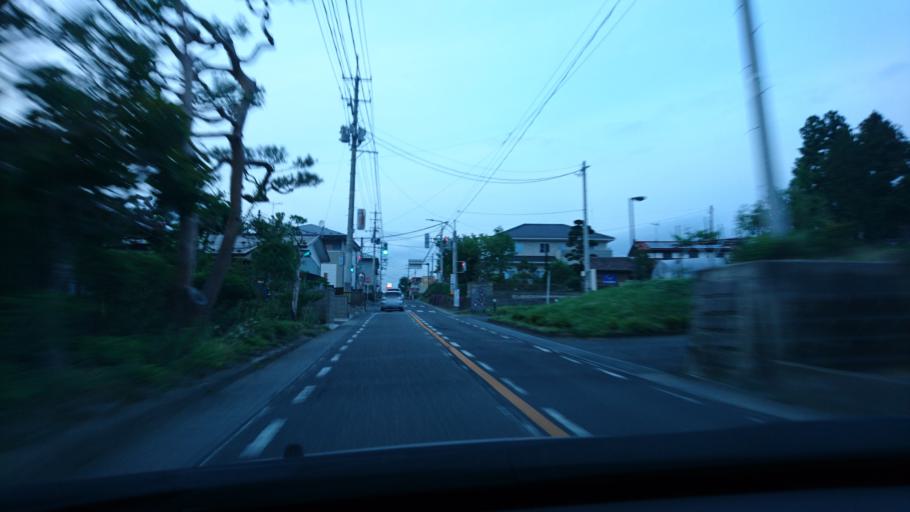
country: JP
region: Iwate
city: Ichinoseki
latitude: 38.8141
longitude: 140.9852
